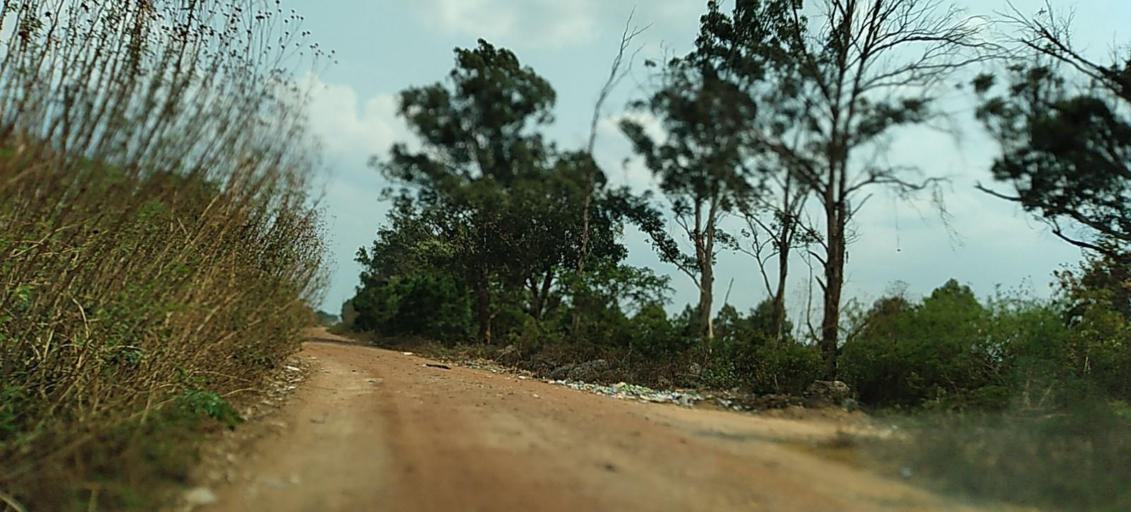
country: ZM
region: Copperbelt
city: Kalulushi
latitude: -12.8313
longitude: 28.0773
